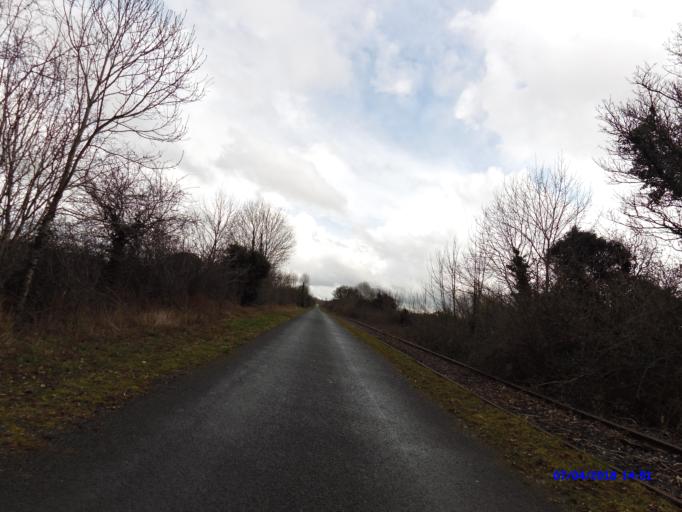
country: IE
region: Leinster
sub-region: An Iarmhi
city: Athlone
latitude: 53.4145
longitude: -7.8558
